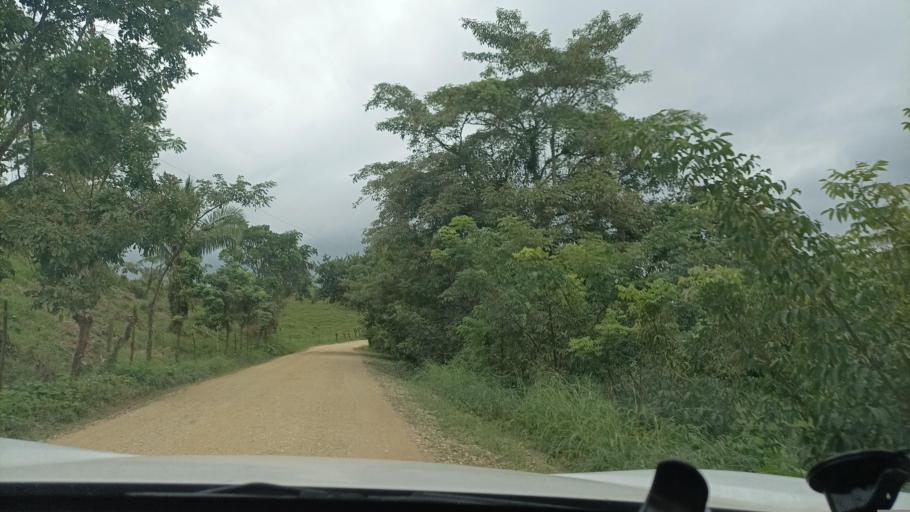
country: MX
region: Veracruz
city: Hidalgotitlan
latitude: 17.6503
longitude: -94.5006
